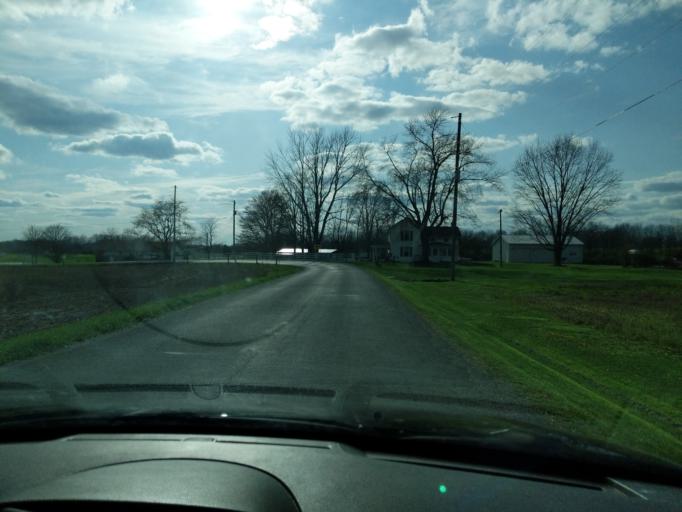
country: US
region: Ohio
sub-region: Champaign County
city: Urbana
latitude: 40.1323
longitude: -83.7278
